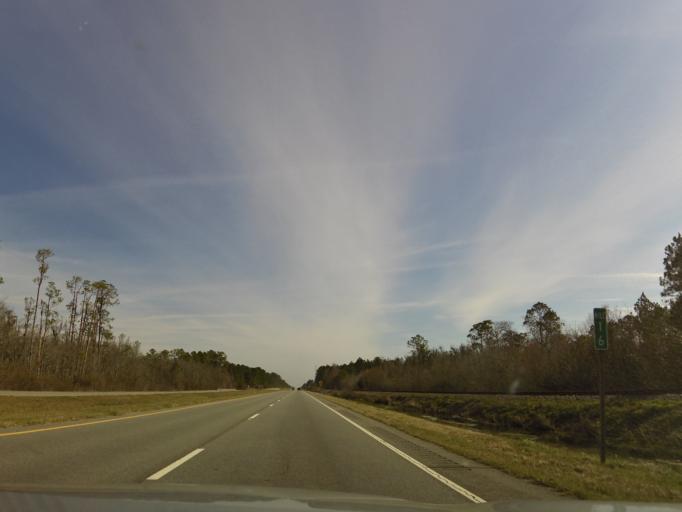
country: US
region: Georgia
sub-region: Lowndes County
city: Valdosta
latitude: 30.8611
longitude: -83.1990
